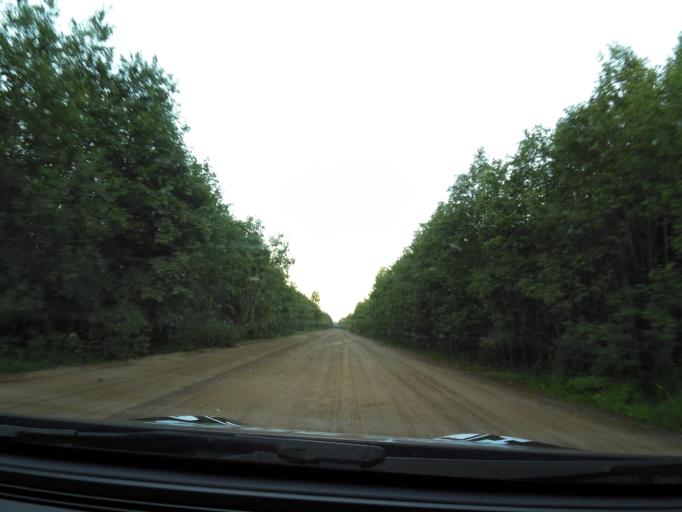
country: RU
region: Leningrad
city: Voznesen'ye
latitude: 60.9275
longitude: 35.4740
